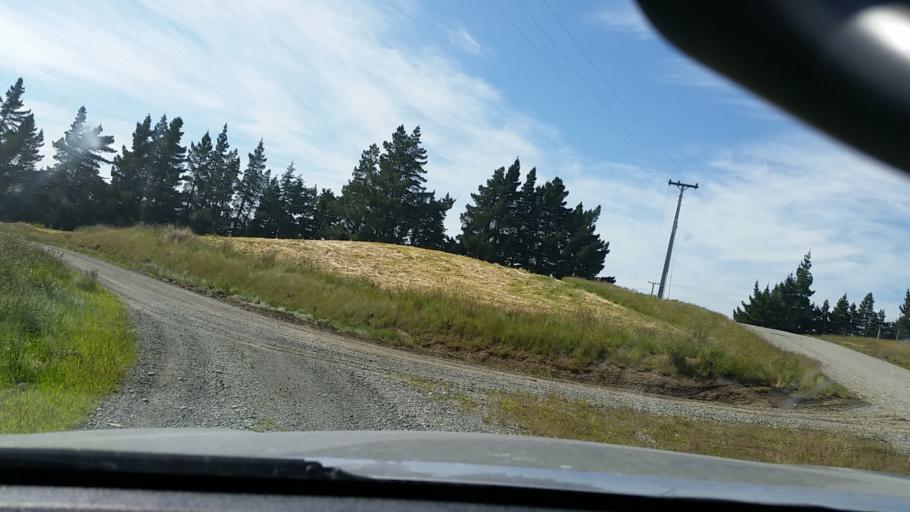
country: NZ
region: Southland
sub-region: Southland District
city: Te Anau
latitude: -45.6324
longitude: 168.1970
